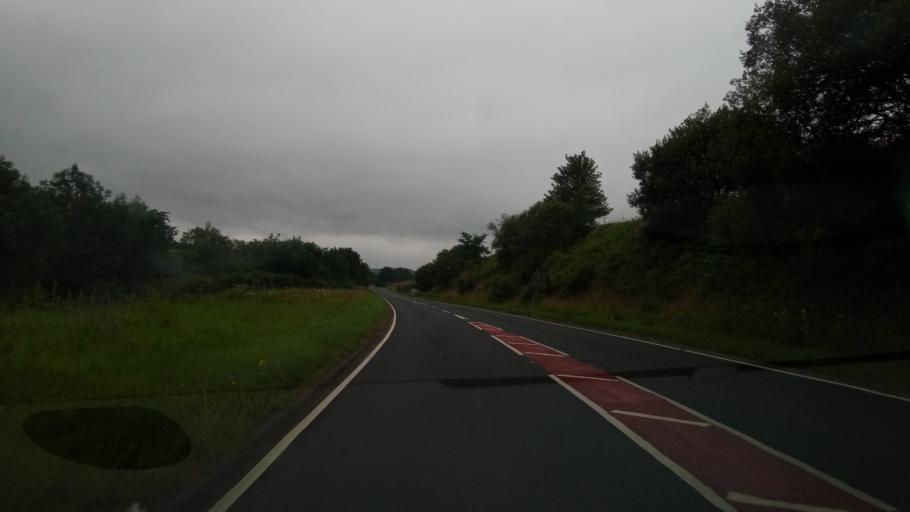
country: GB
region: Scotland
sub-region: The Scottish Borders
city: Hawick
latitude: 55.3828
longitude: -2.8694
